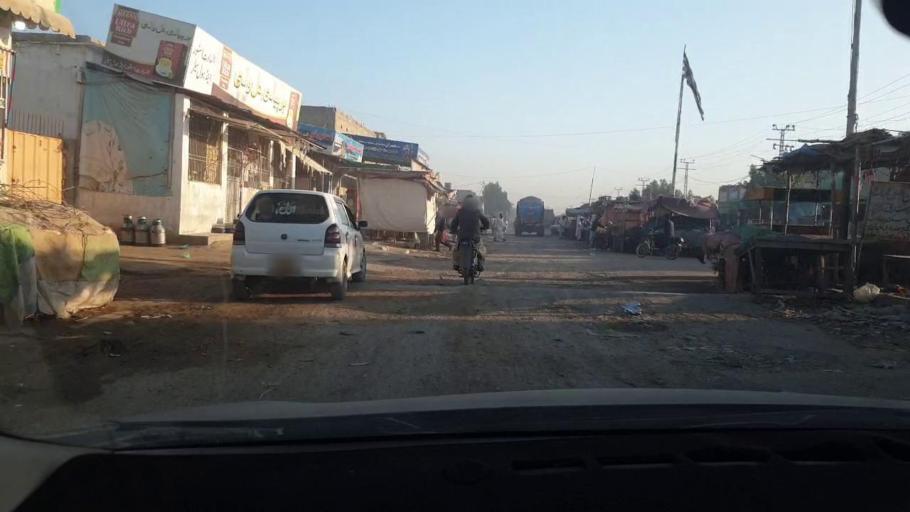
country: PK
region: Sindh
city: Malir Cantonment
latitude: 25.0124
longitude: 67.1681
